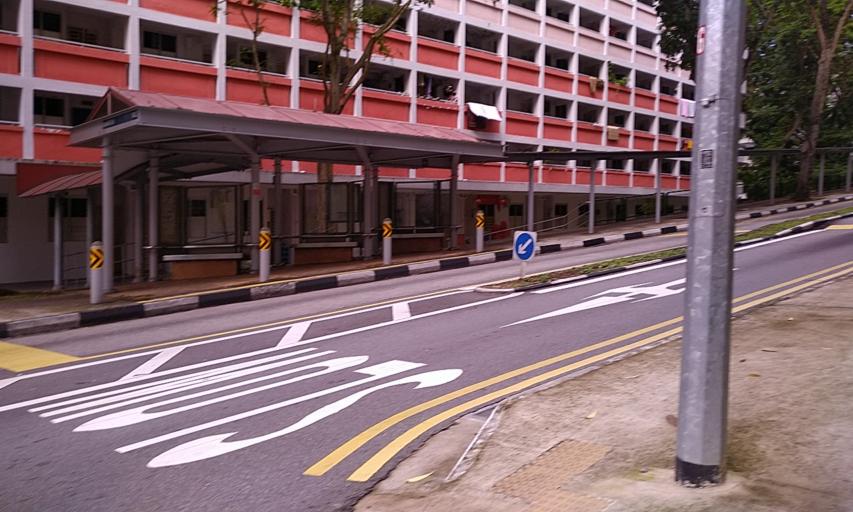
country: SG
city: Singapore
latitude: 1.2876
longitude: 103.8164
